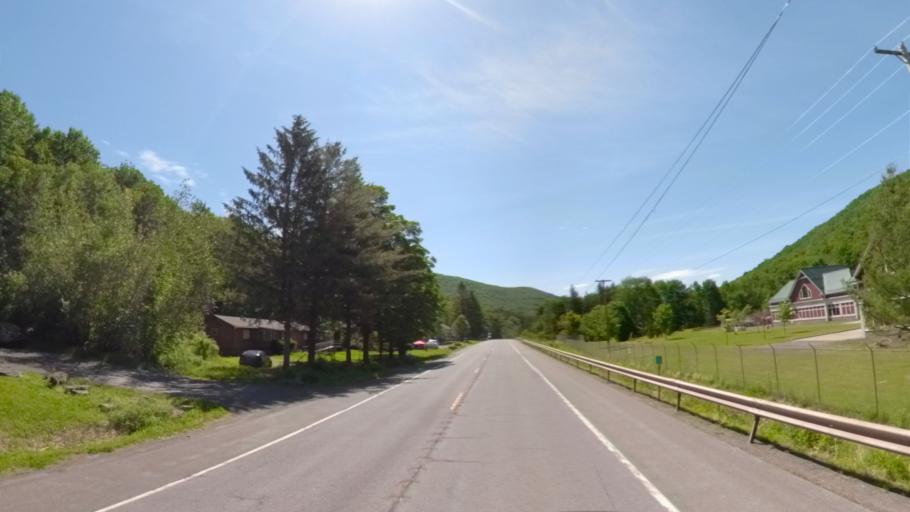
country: US
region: New York
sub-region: Ulster County
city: Shokan
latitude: 42.1226
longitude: -74.4629
